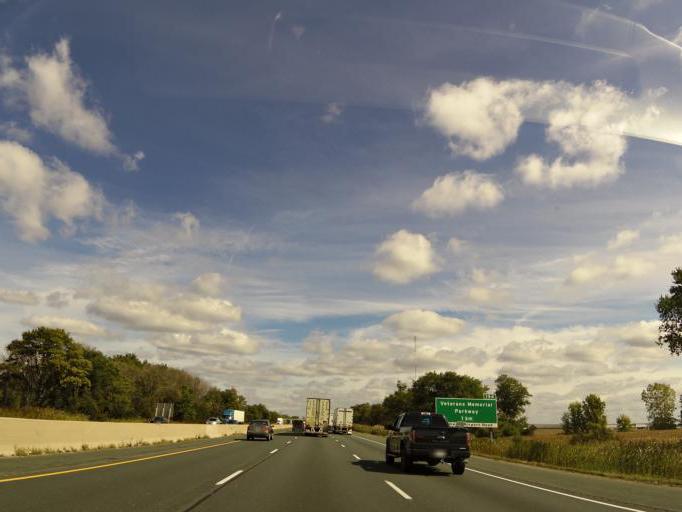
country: CA
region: Ontario
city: Dorchester
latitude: 42.9411
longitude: -81.1445
